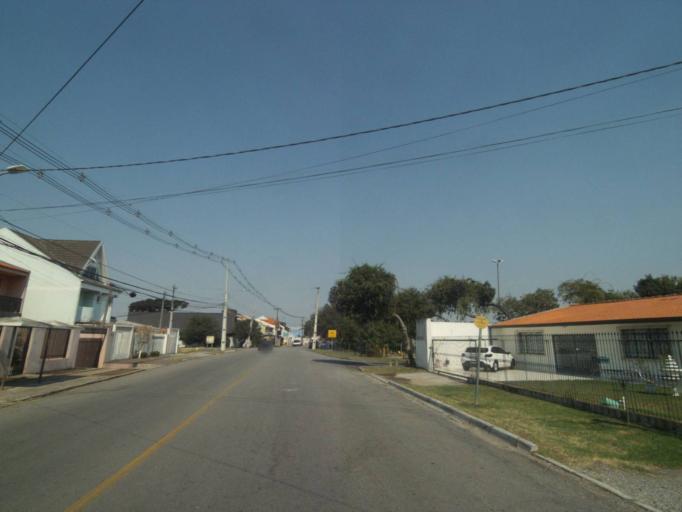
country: BR
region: Parana
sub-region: Sao Jose Dos Pinhais
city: Sao Jose dos Pinhais
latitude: -25.4943
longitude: -49.2627
